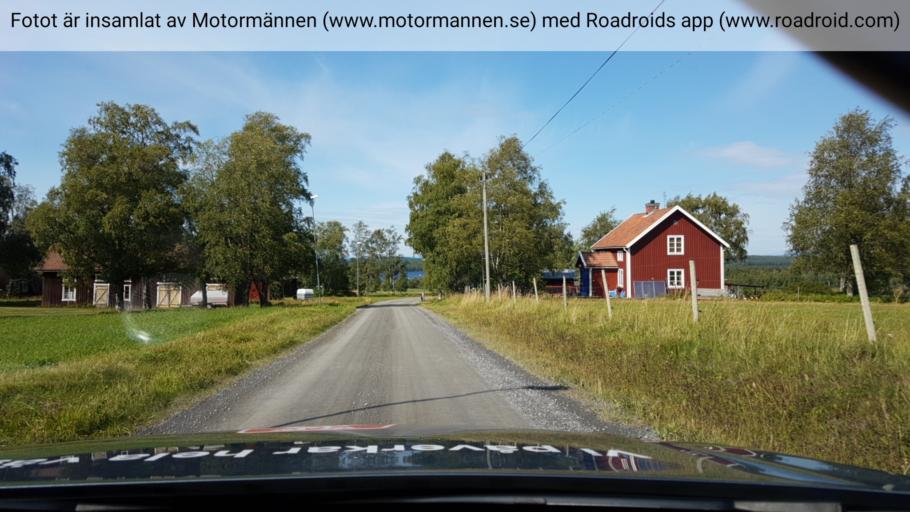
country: SE
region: Jaemtland
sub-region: OEstersunds Kommun
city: Ostersund
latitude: 63.1323
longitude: 14.4681
